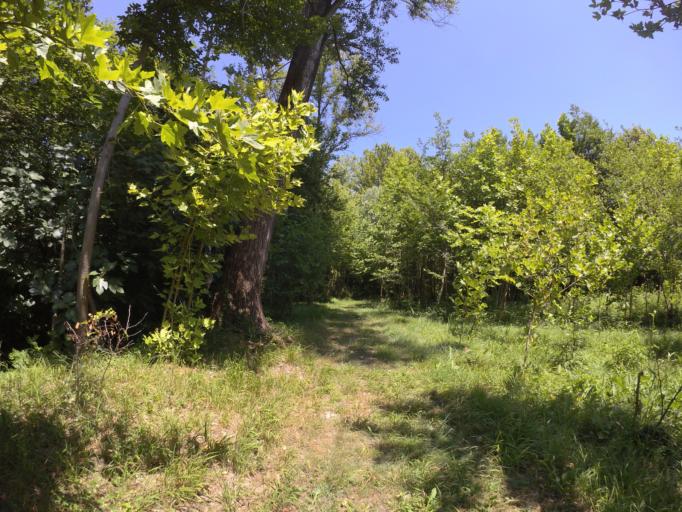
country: IT
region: Friuli Venezia Giulia
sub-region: Provincia di Udine
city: Bertiolo
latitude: 45.9270
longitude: 13.0832
